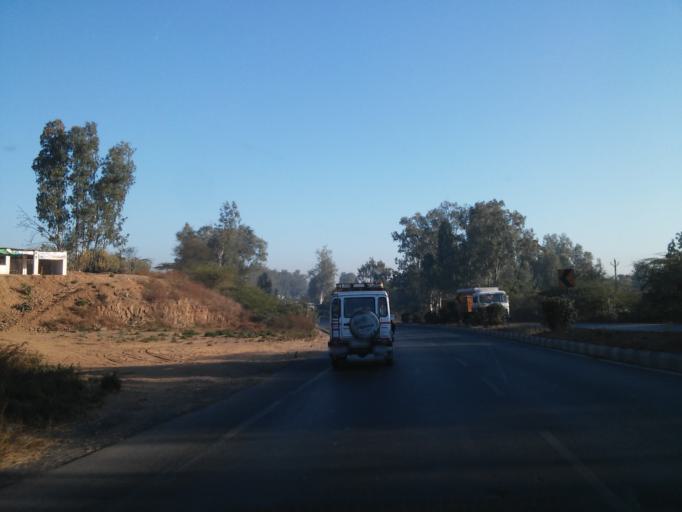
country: IN
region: Rajasthan
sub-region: Dungarpur
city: Dungarpur
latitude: 23.8755
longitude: 73.5304
